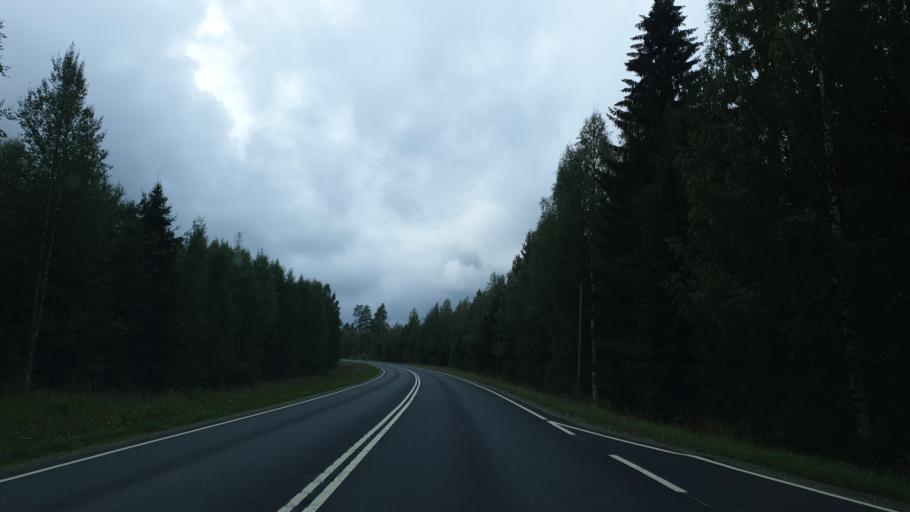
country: FI
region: Northern Savo
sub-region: Kuopio
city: Nilsiae
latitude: 63.2377
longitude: 28.2557
